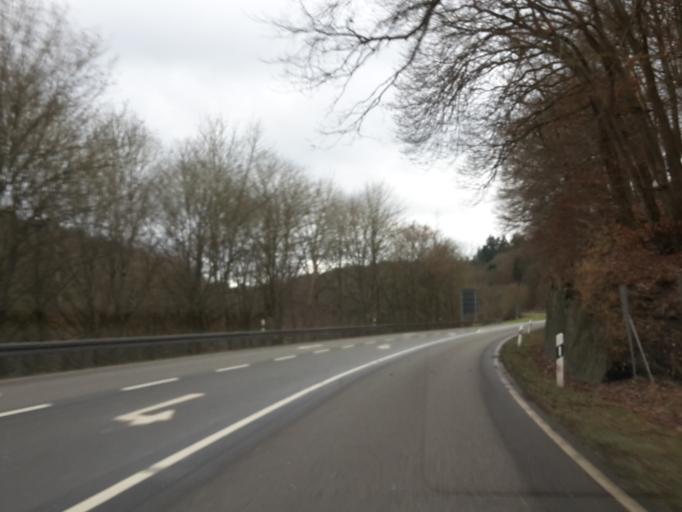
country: DE
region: Hesse
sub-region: Regierungsbezirk Darmstadt
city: Idstein
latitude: 50.1974
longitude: 8.2445
